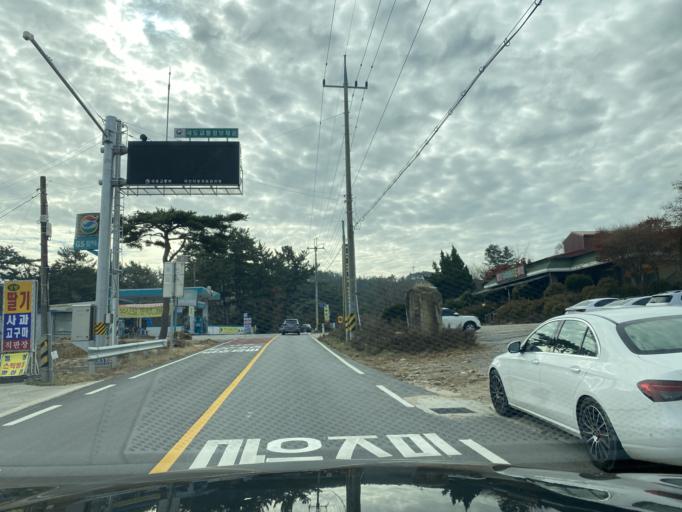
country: KR
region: Chungcheongnam-do
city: Hongsung
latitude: 36.6740
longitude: 126.6425
